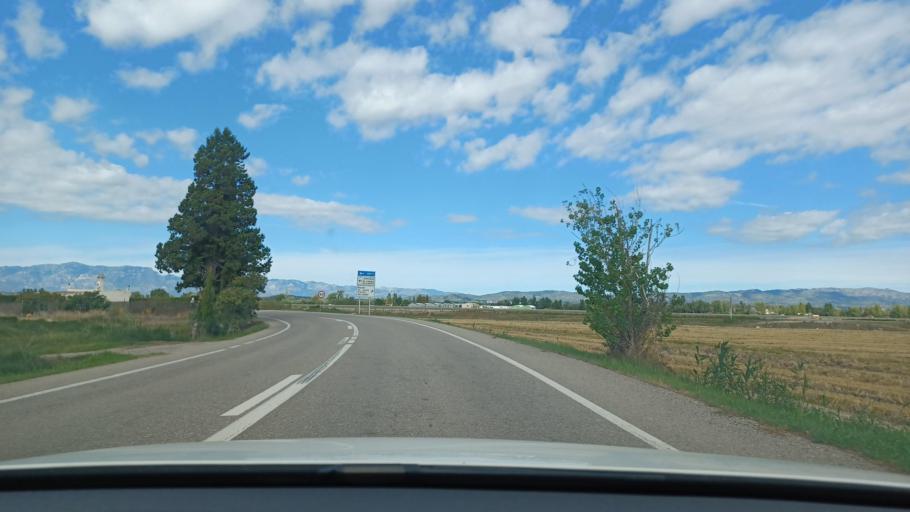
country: ES
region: Catalonia
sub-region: Provincia de Tarragona
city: Amposta
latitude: 40.7062
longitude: 0.6410
